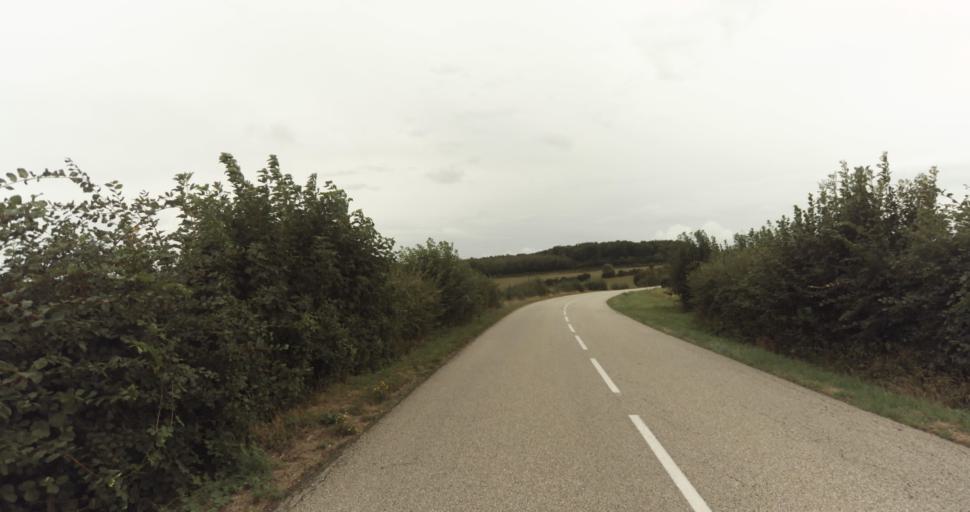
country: FR
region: Lower Normandy
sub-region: Departement de l'Orne
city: Gace
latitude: 48.7998
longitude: 0.3180
